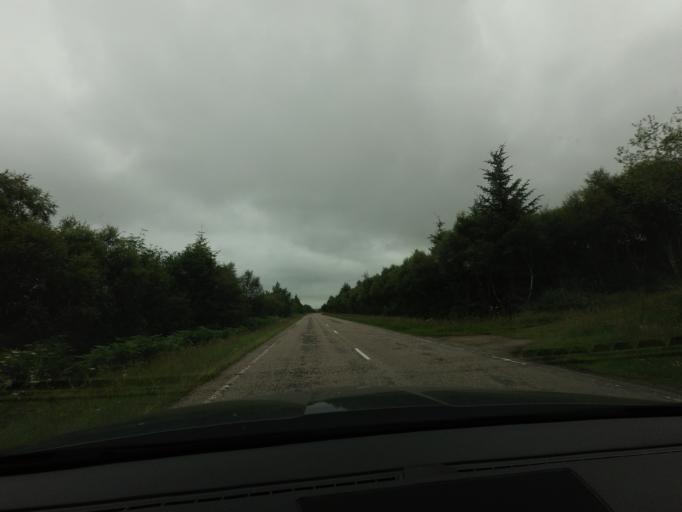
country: GB
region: Scotland
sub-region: Highland
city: Alness
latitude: 57.9914
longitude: -4.4039
